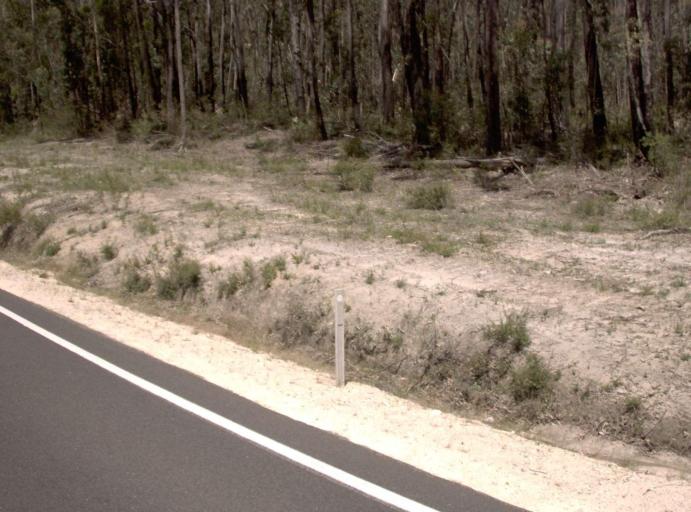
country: AU
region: New South Wales
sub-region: Bombala
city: Bombala
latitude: -37.5656
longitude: 149.2247
